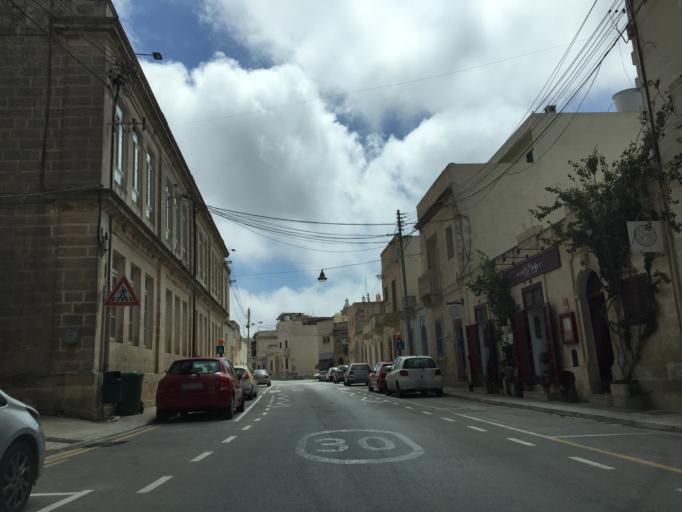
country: MT
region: Dingli
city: Dingli
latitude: 35.8623
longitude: 14.3848
